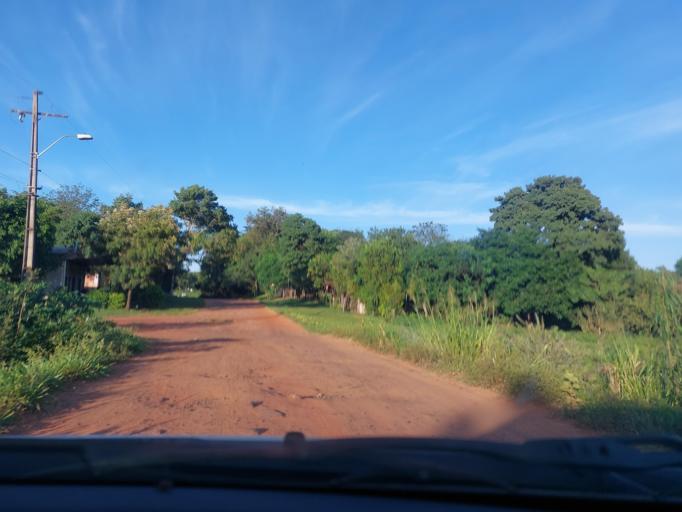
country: PY
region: San Pedro
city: Itacurubi del Rosario
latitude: -24.5643
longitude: -56.5934
